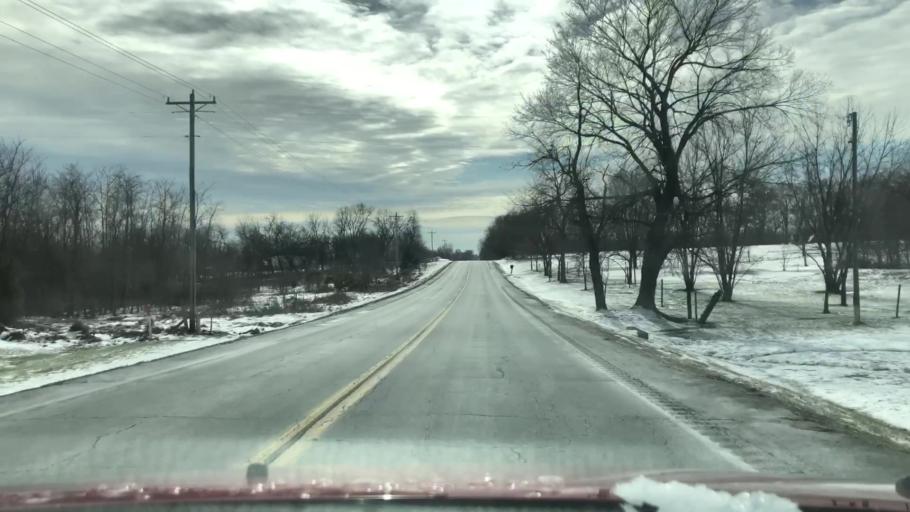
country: US
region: Missouri
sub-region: Jackson County
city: Lone Jack
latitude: 38.8800
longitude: -94.1351
